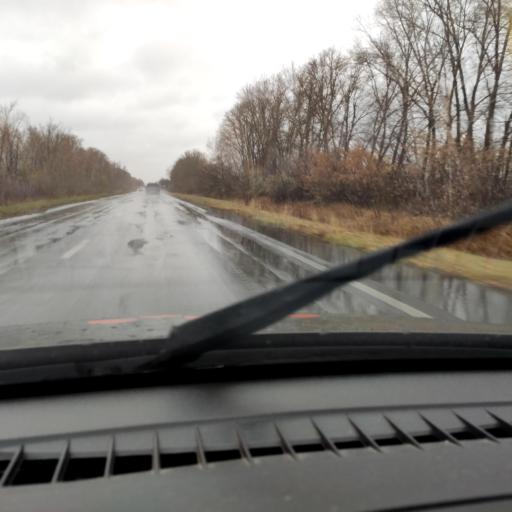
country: RU
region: Samara
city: Tol'yatti
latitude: 53.6111
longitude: 49.3159
